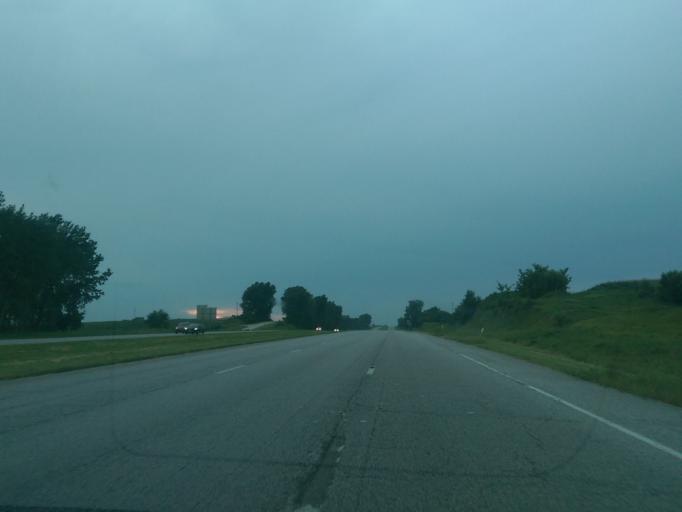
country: US
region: Missouri
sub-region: Holt County
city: Oregon
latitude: 40.0469
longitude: -95.1416
